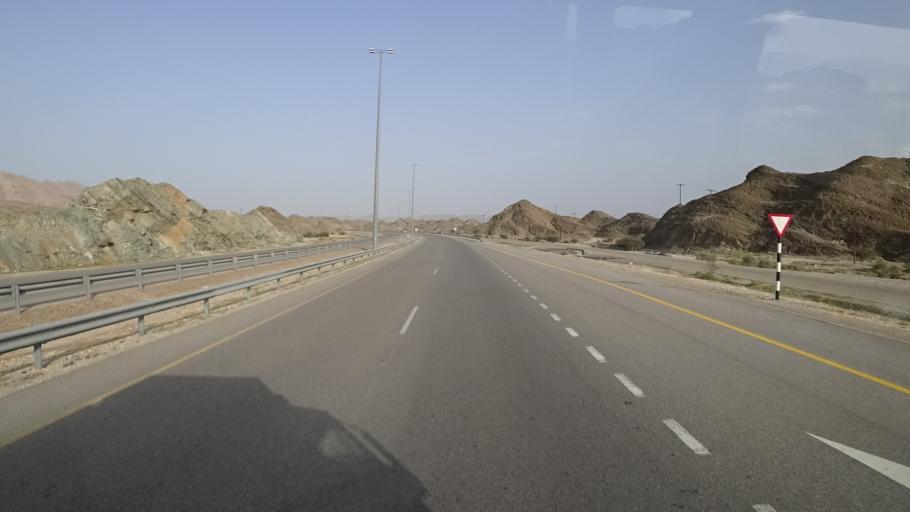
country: OM
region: Muhafazat Masqat
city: Bawshar
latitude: 23.3439
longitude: 58.5610
